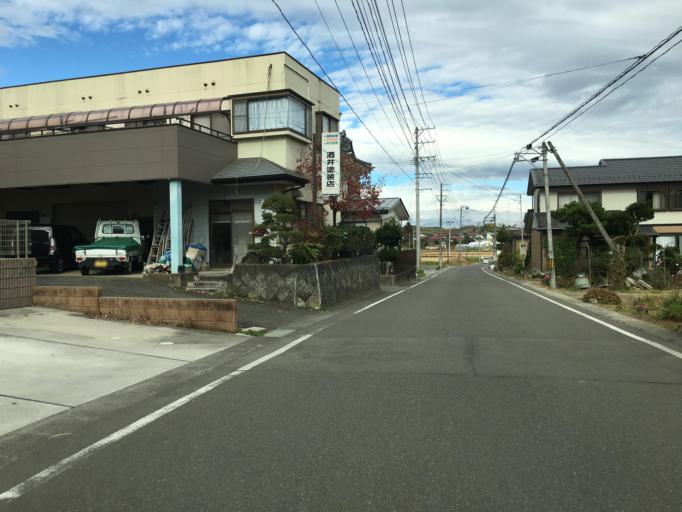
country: JP
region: Fukushima
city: Nihommatsu
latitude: 37.6197
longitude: 140.4609
